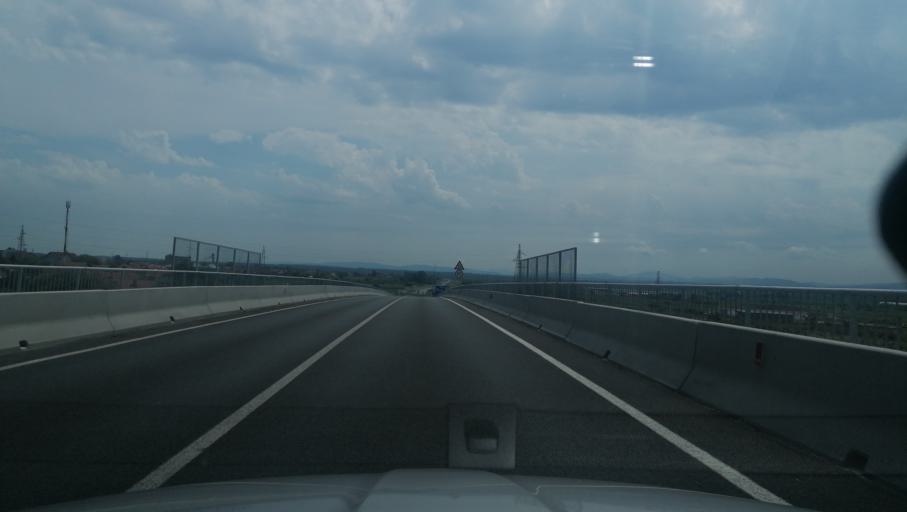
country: BA
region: Brcko
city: Brka
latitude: 44.8635
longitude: 18.7577
